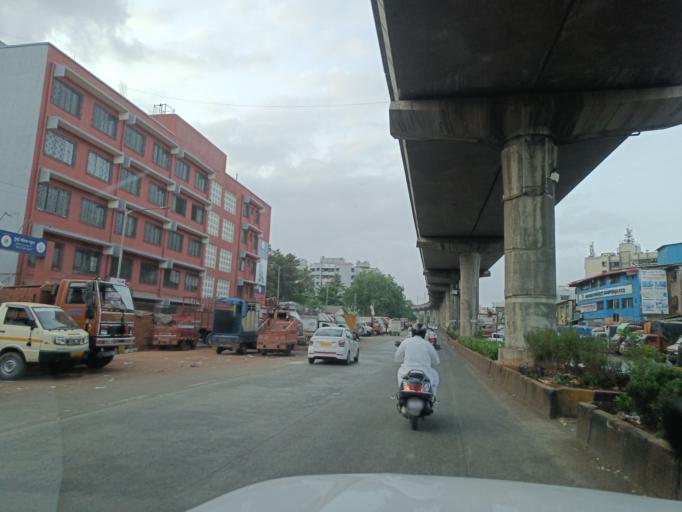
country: IN
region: Maharashtra
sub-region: Mumbai Suburban
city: Powai
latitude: 19.1003
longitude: 72.8916
